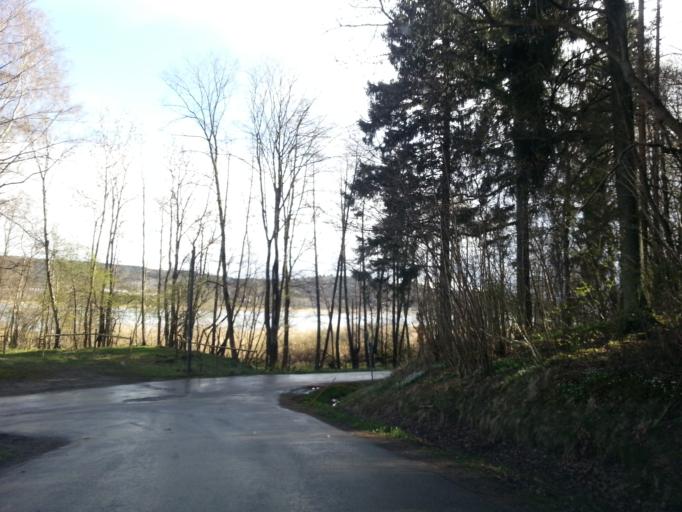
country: SE
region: Vaestra Goetaland
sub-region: Kungalvs Kommun
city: Diserod
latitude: 57.8786
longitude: 12.0222
